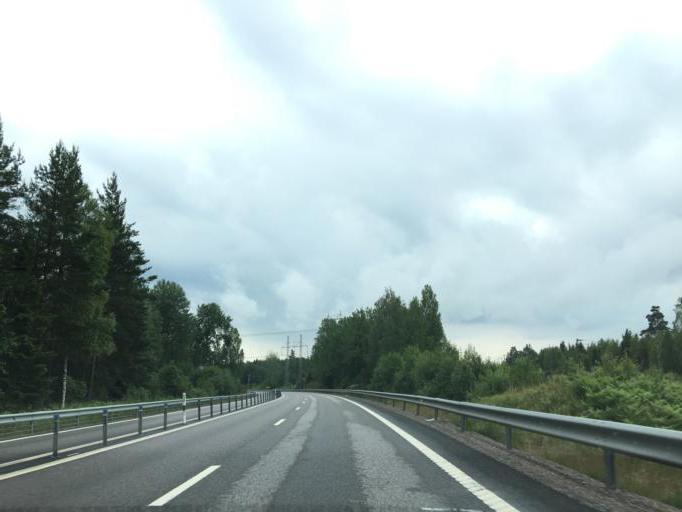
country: SE
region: OEstergoetland
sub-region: Norrkopings Kommun
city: Jursla
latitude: 58.8087
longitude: 16.1516
